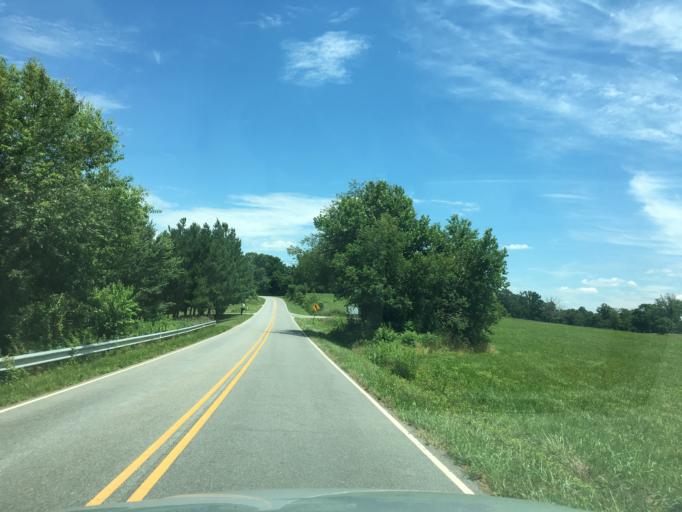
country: US
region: North Carolina
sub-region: Burke County
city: Glen Alpine
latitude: 35.6503
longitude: -81.7849
